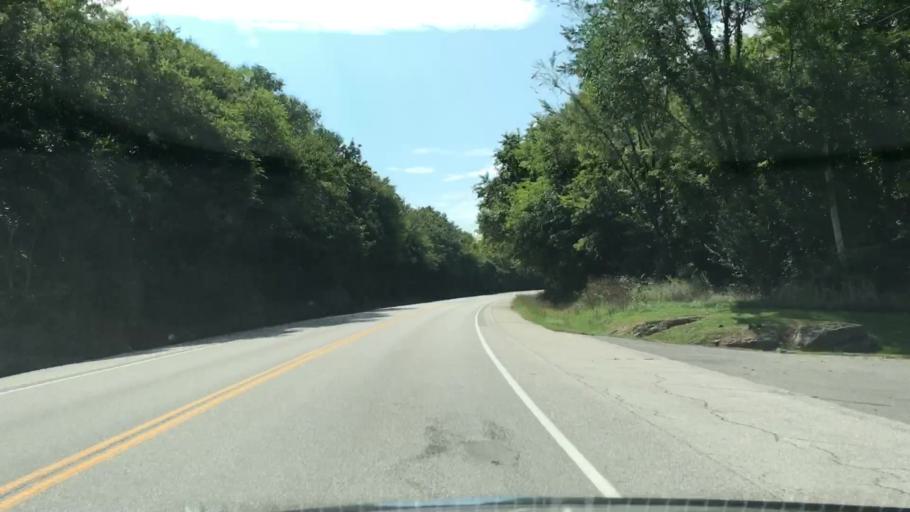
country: US
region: Tennessee
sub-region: Smith County
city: Carthage
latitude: 36.3313
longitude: -86.0234
